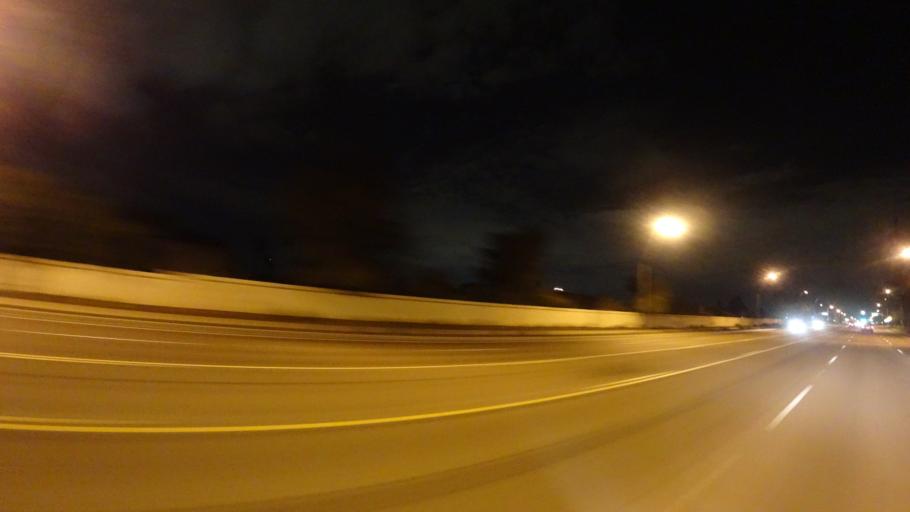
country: US
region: Arizona
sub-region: Maricopa County
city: Guadalupe
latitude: 33.3546
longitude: -111.9112
